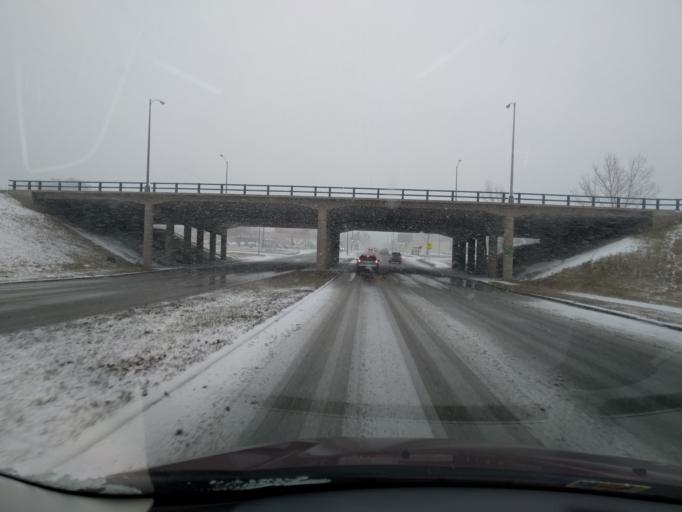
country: US
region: Wisconsin
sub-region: Milwaukee County
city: Glendale
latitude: 43.1193
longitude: -87.9682
